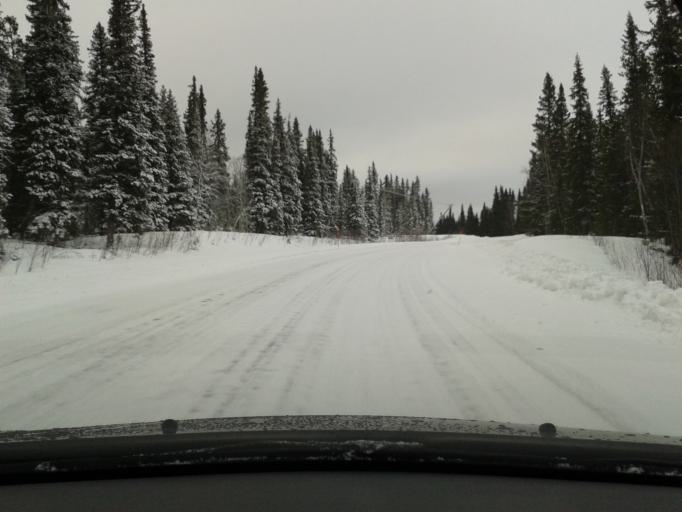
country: SE
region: Vaesterbotten
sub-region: Vilhelmina Kommun
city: Sjoberg
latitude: 65.2282
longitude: 15.8961
